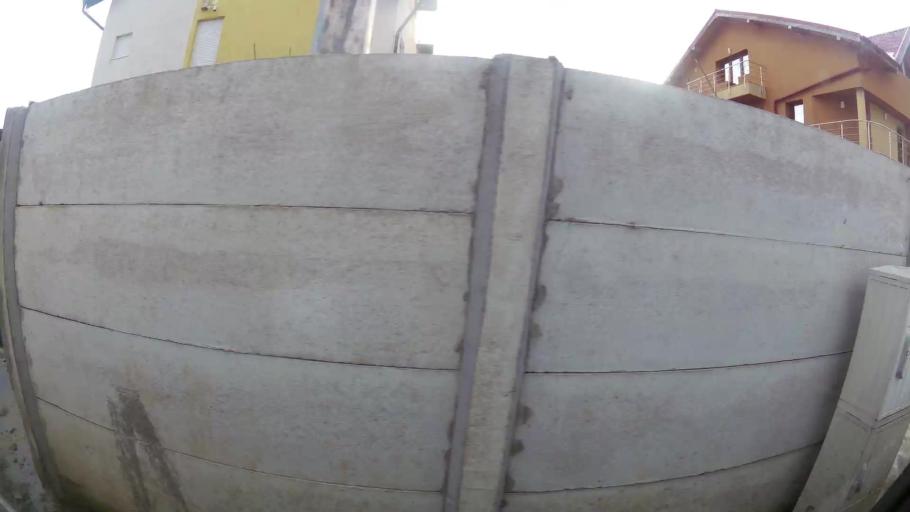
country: RO
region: Ilfov
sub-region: Comuna Popesti-Leordeni
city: Popesti-Leordeni
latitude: 44.4028
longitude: 26.1826
